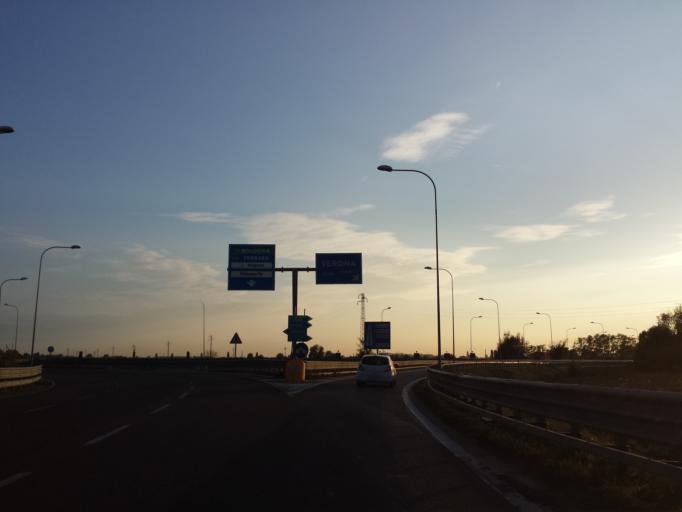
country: IT
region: Veneto
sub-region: Provincia di Rovigo
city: Bosaro
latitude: 45.0264
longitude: 11.7725
